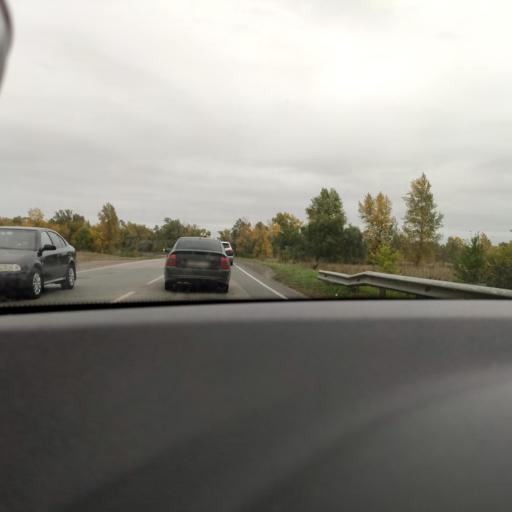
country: RU
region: Samara
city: Krasnyy Yar
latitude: 53.4964
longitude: 50.3639
